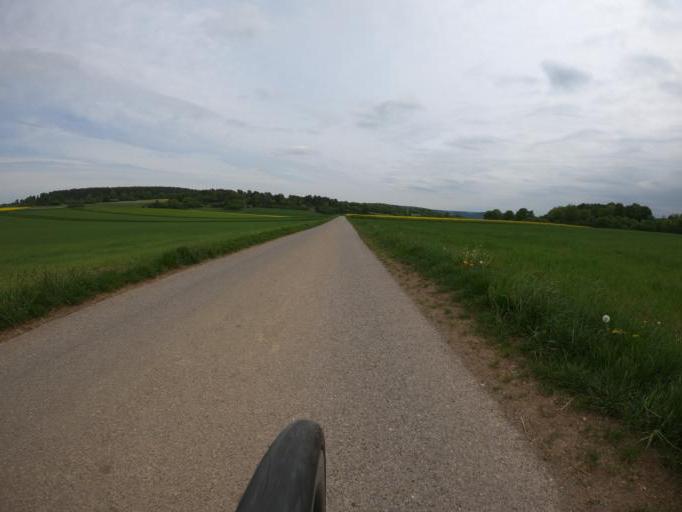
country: DE
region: Baden-Wuerttemberg
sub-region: Regierungsbezirk Stuttgart
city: Aidlingen
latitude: 48.6900
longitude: 8.8693
